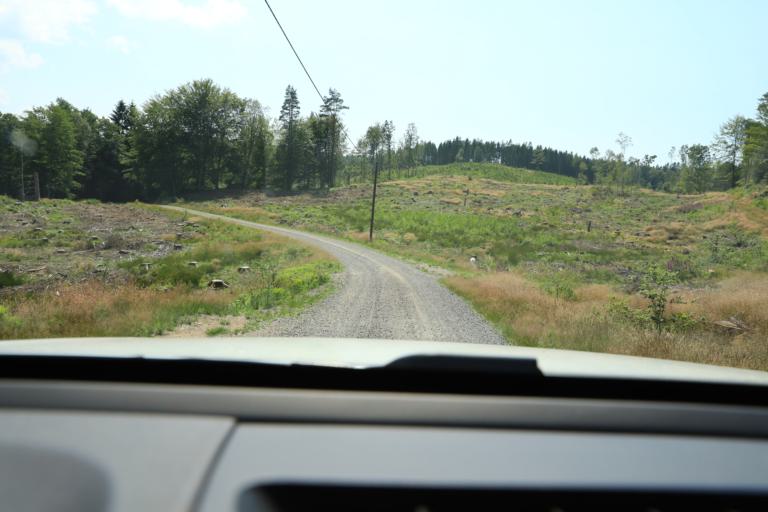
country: SE
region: Halland
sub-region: Varbergs Kommun
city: Veddige
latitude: 57.2130
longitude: 12.3496
